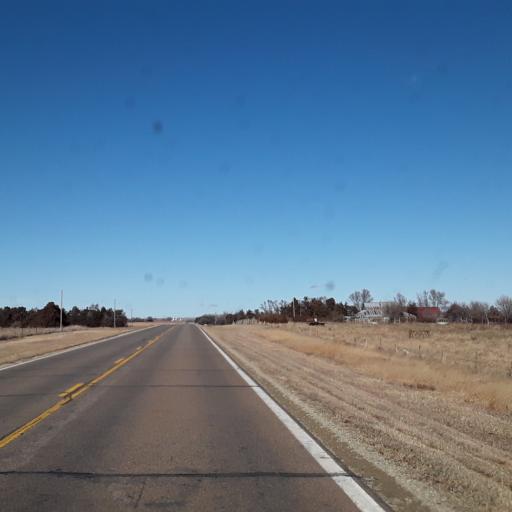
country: US
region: Kansas
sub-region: Lincoln County
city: Lincoln
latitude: 38.9760
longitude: -98.1512
